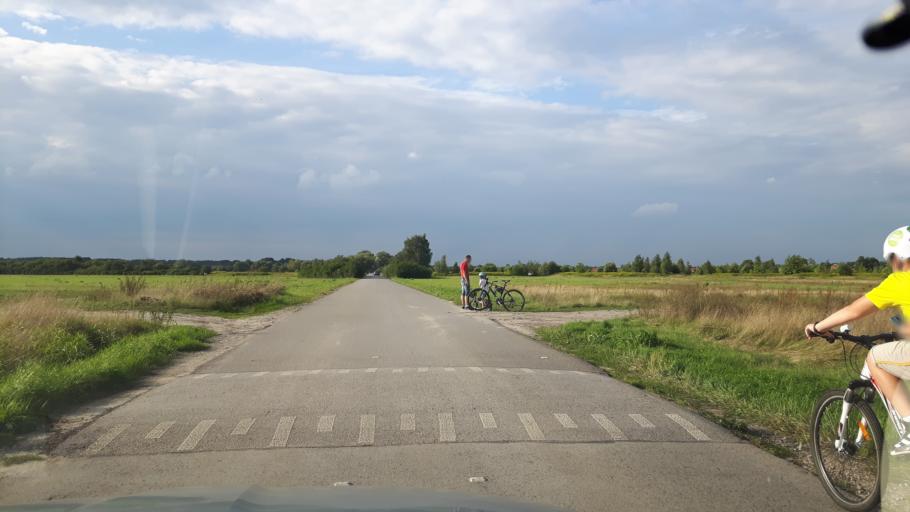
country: PL
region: Masovian Voivodeship
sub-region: Powiat wolominski
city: Marki
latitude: 52.3301
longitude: 21.0758
